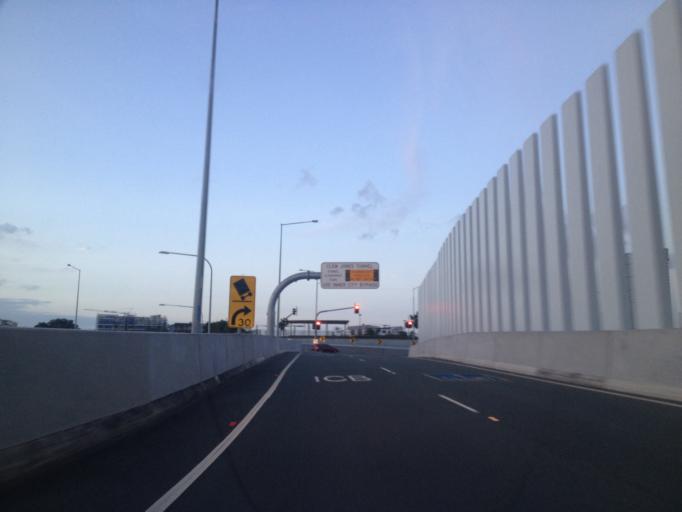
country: AU
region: Queensland
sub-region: Brisbane
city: Windsor
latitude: -27.4426
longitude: 153.0310
